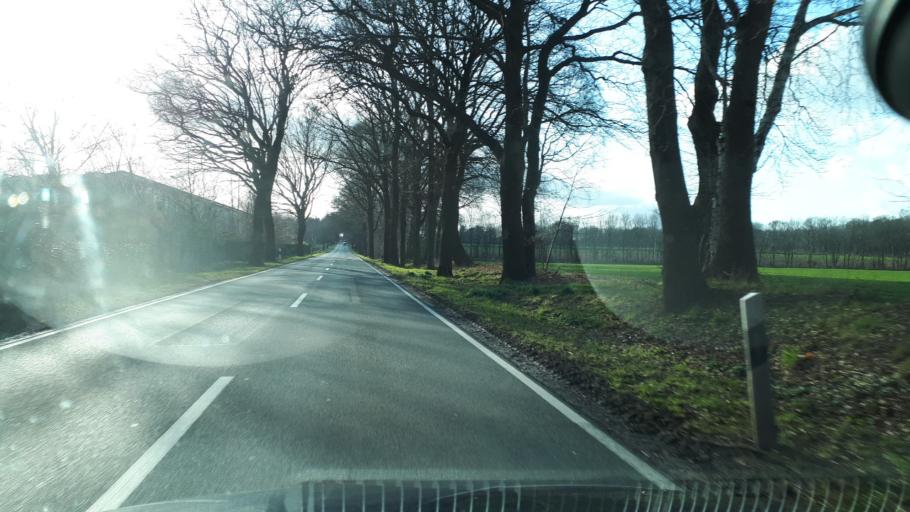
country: DE
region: Lower Saxony
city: Molbergen
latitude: 52.8551
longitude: 7.9467
